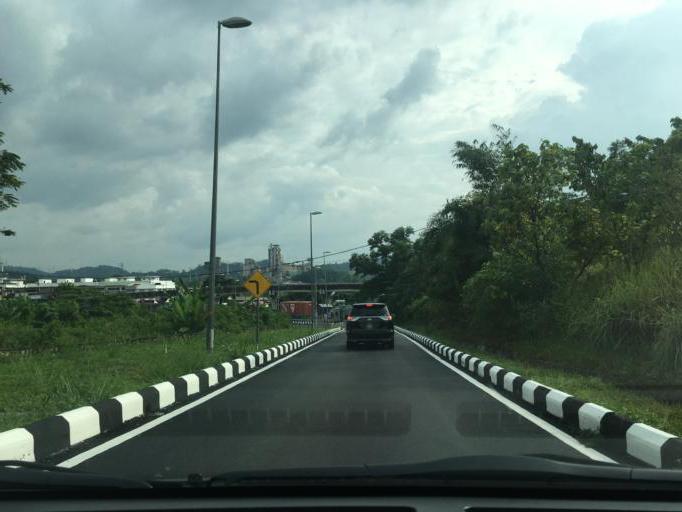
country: MY
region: Selangor
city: Rawang
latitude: 3.3171
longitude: 101.5781
